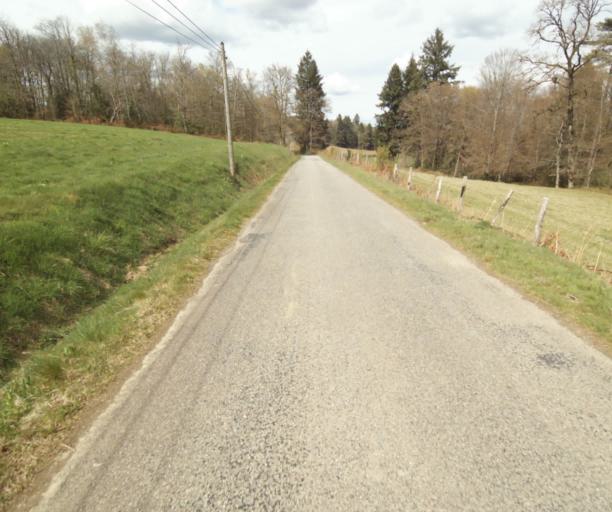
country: FR
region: Limousin
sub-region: Departement de la Correze
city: Laguenne
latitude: 45.2332
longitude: 1.8683
